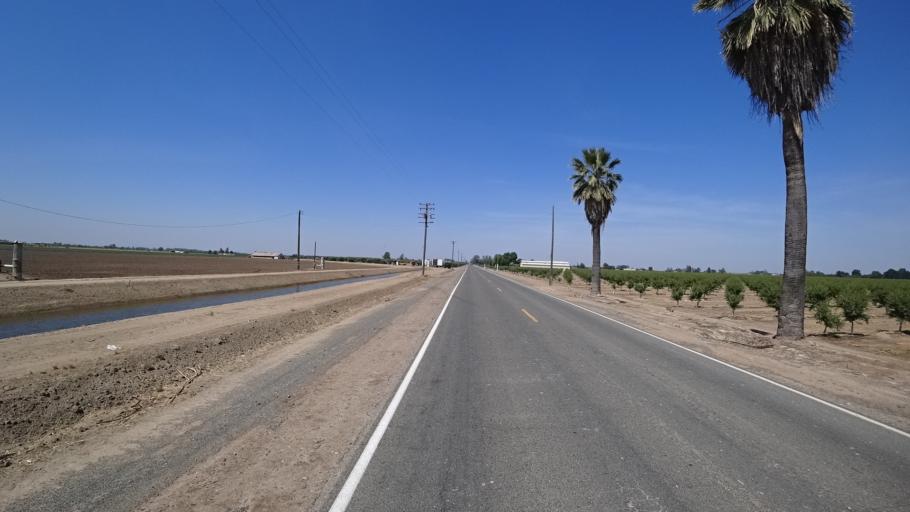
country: US
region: California
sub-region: Fresno County
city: Riverdale
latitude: 36.4020
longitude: -119.7877
